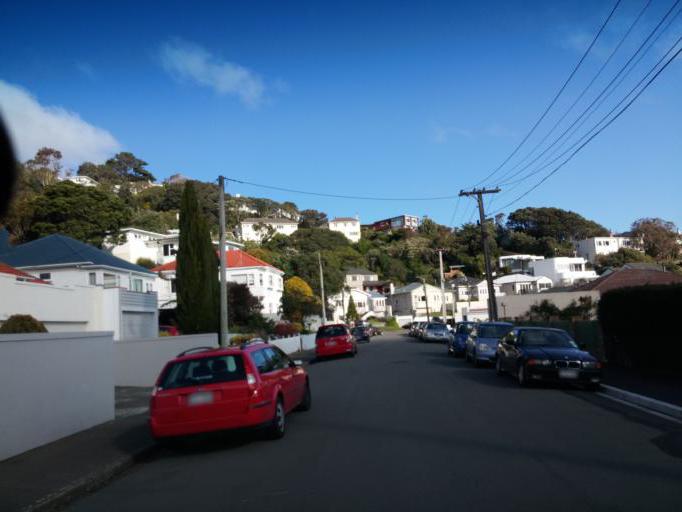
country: NZ
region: Wellington
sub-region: Wellington City
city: Wellington
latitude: -41.3245
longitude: 174.8257
